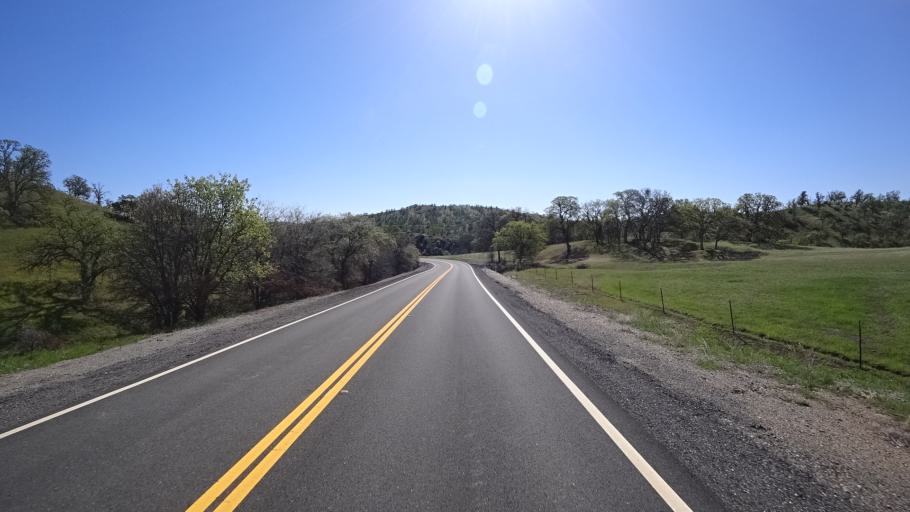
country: US
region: California
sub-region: Glenn County
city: Orland
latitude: 39.6545
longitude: -122.5874
